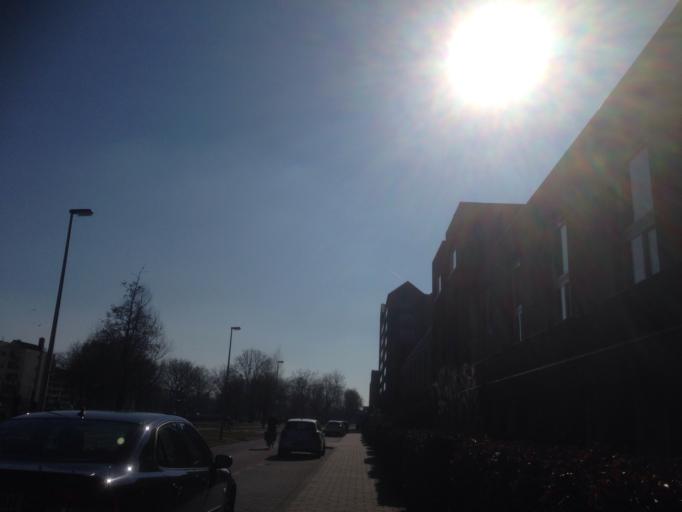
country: NL
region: Utrecht
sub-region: Gemeente Utrecht
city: Lunetten
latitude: 52.0678
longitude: 5.1226
